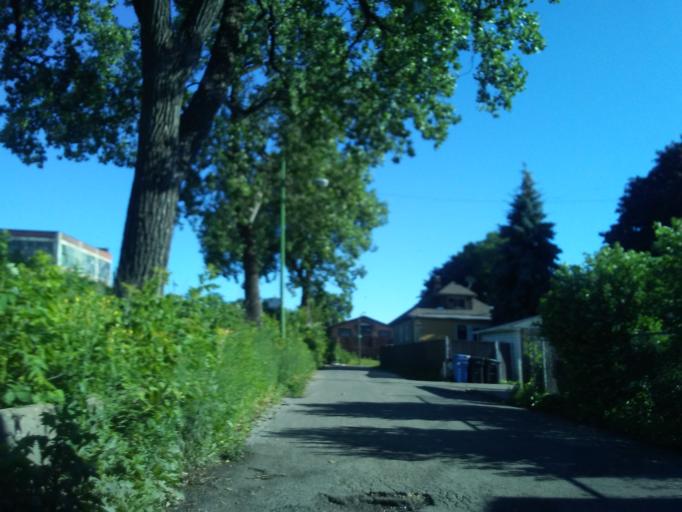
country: US
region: Illinois
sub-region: Cook County
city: Oak Park
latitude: 41.9195
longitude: -87.7417
